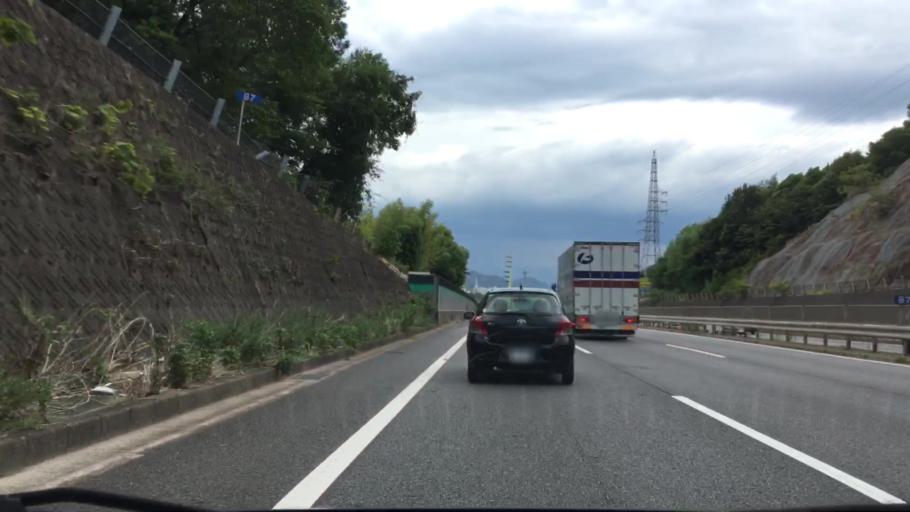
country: JP
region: Hyogo
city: Himeji
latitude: 34.8029
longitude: 134.7062
